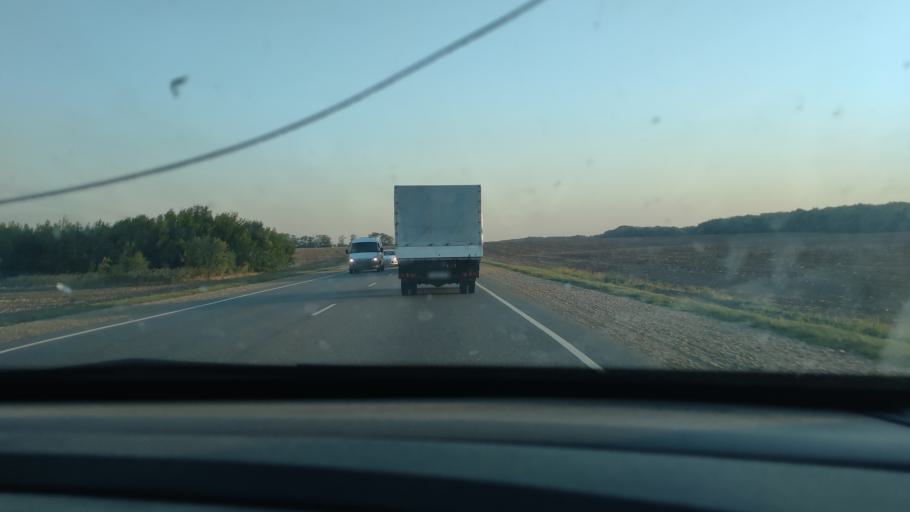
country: RU
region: Krasnodarskiy
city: Bryukhovetskaya
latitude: 45.7501
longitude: 38.9875
